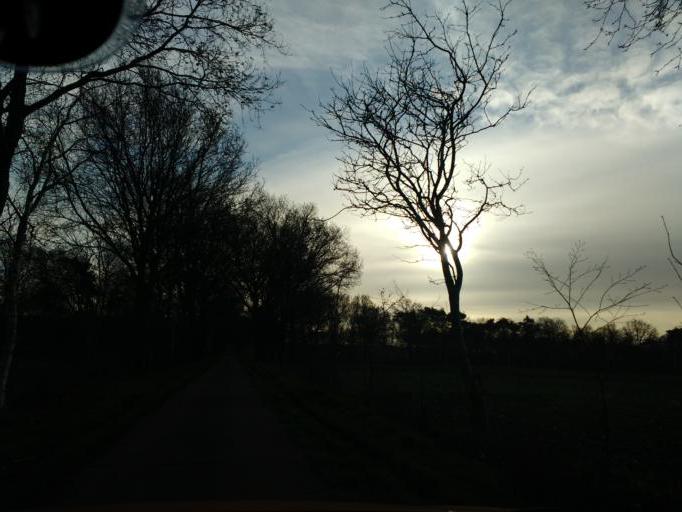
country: DE
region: Lower Saxony
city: Hatten
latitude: 53.1216
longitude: 8.3832
